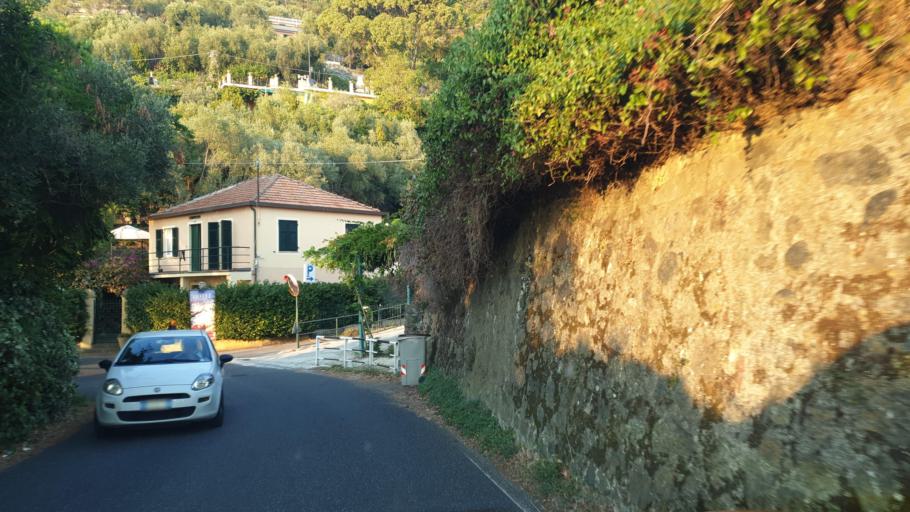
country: IT
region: Liguria
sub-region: Provincia di La Spezia
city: Bonassola
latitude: 44.1812
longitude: 9.5866
